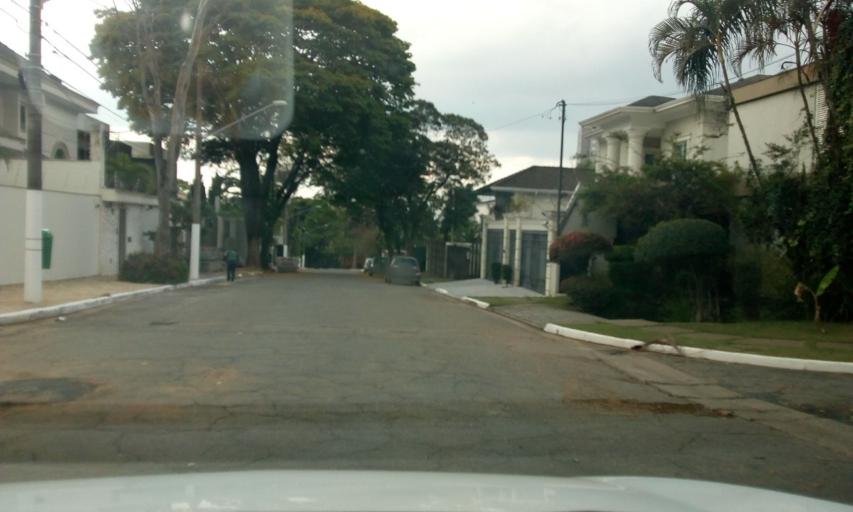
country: BR
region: Sao Paulo
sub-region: Sao Paulo
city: Sao Paulo
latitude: -23.6043
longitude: -46.6528
